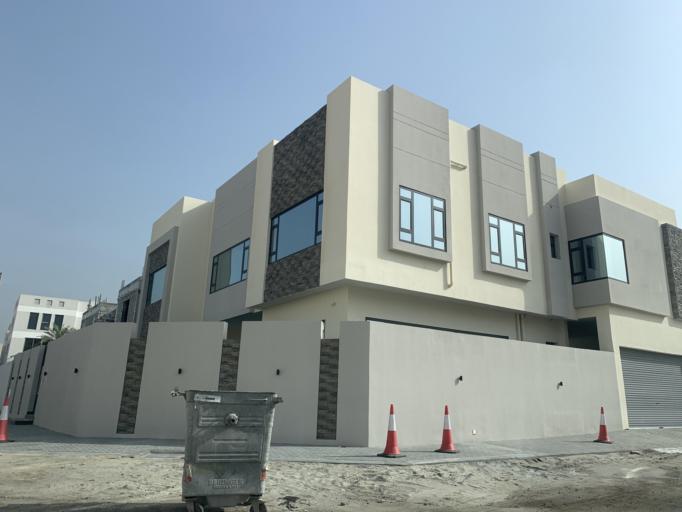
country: BH
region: Northern
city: Madinat `Isa
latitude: 26.1883
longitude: 50.5644
